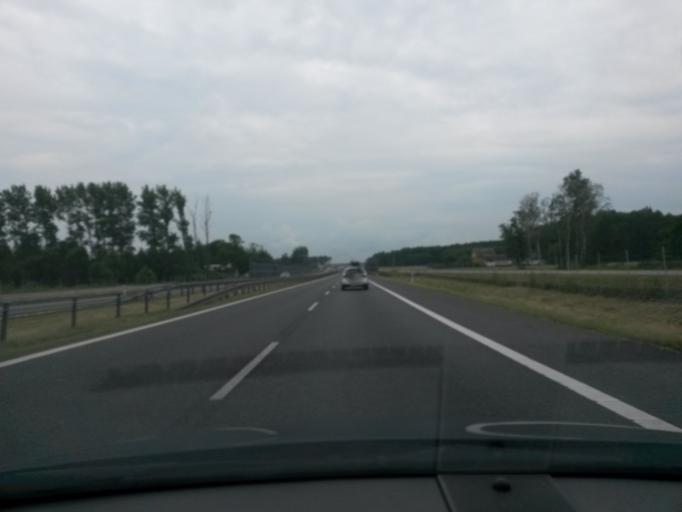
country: PL
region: Masovian Voivodeship
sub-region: Powiat zyrardowski
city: Mszczonow
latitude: 51.9579
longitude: 20.4968
